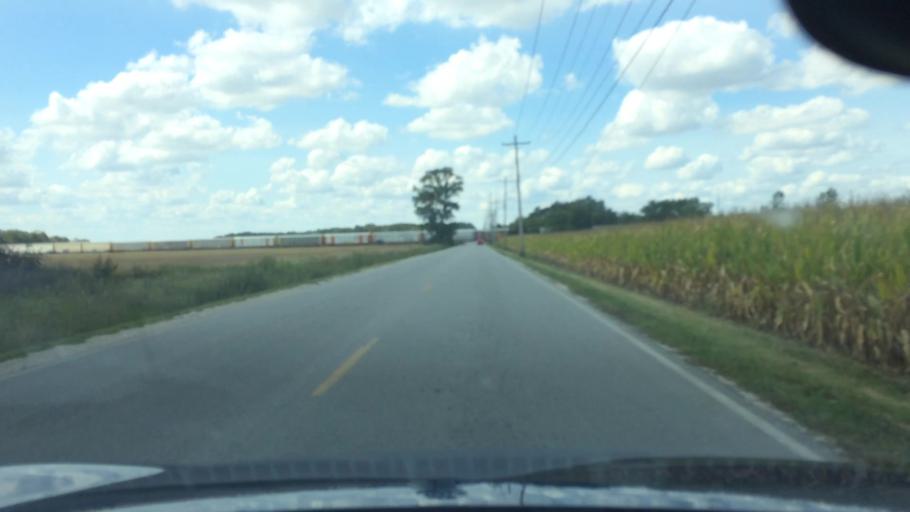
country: US
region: Ohio
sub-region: Wood County
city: Perrysburg
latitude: 41.5219
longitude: -83.5693
